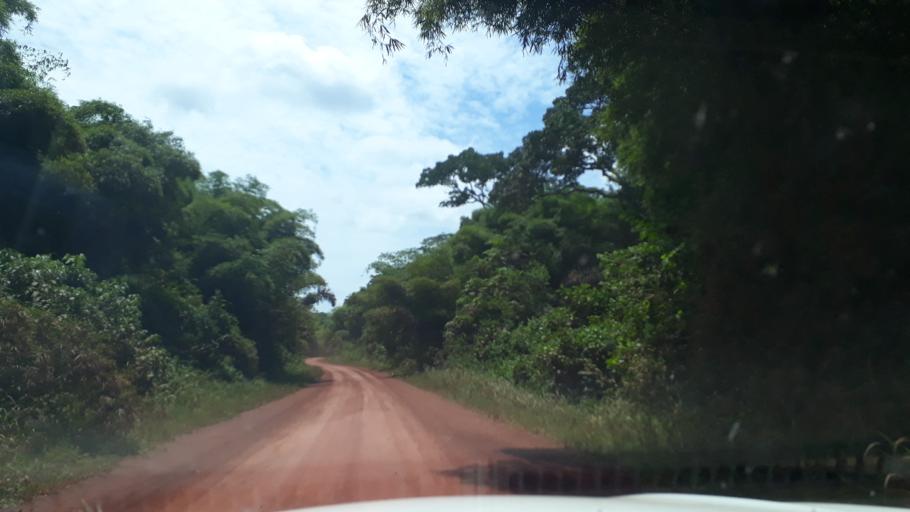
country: CD
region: Eastern Province
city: Kisangani
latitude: 0.5593
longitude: 25.8524
